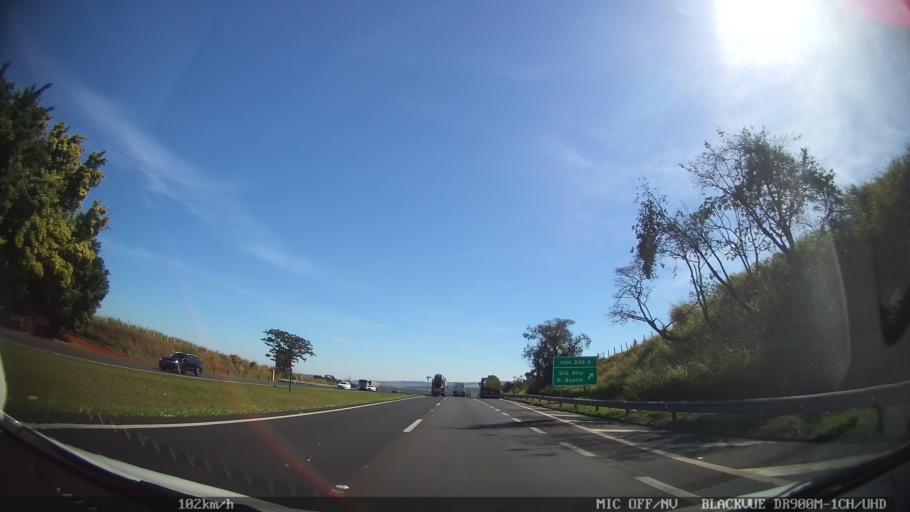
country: BR
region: Sao Paulo
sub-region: Santa Rita Do Passa Quatro
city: Santa Rita do Passa Quatro
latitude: -21.7588
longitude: -47.5601
